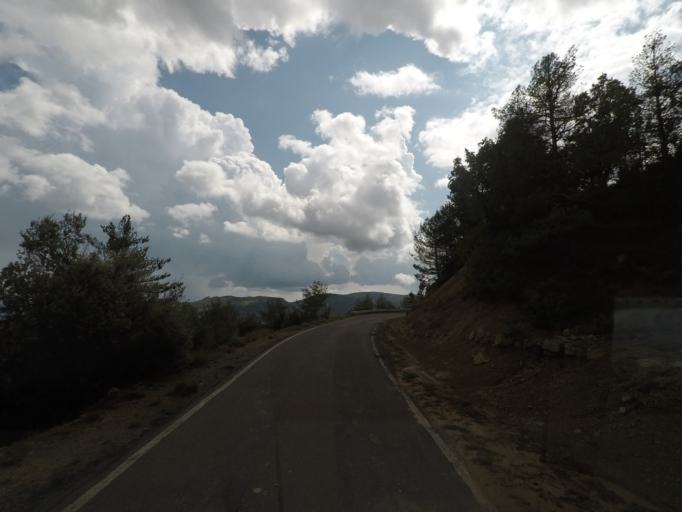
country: ES
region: Aragon
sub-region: Provincia de Huesca
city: Boltana
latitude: 42.4118
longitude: -0.0001
